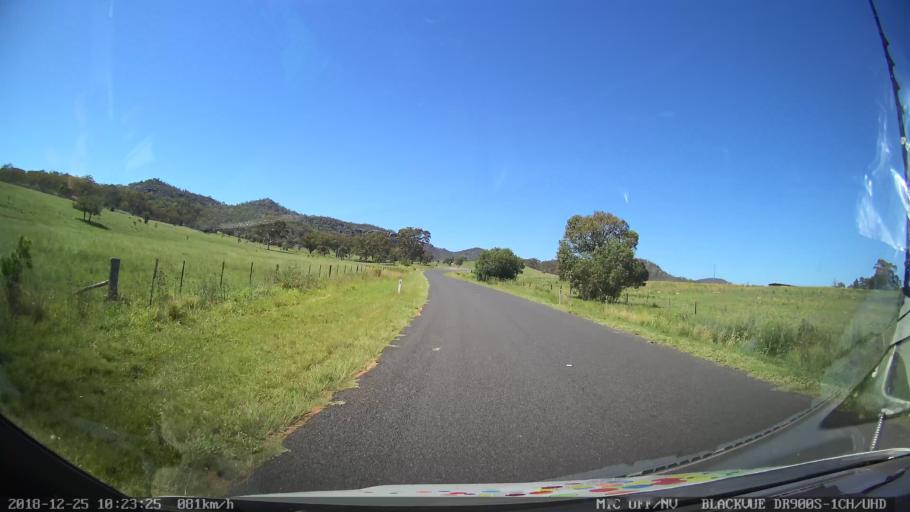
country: AU
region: New South Wales
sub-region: Muswellbrook
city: Denman
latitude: -32.3854
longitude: 150.5231
